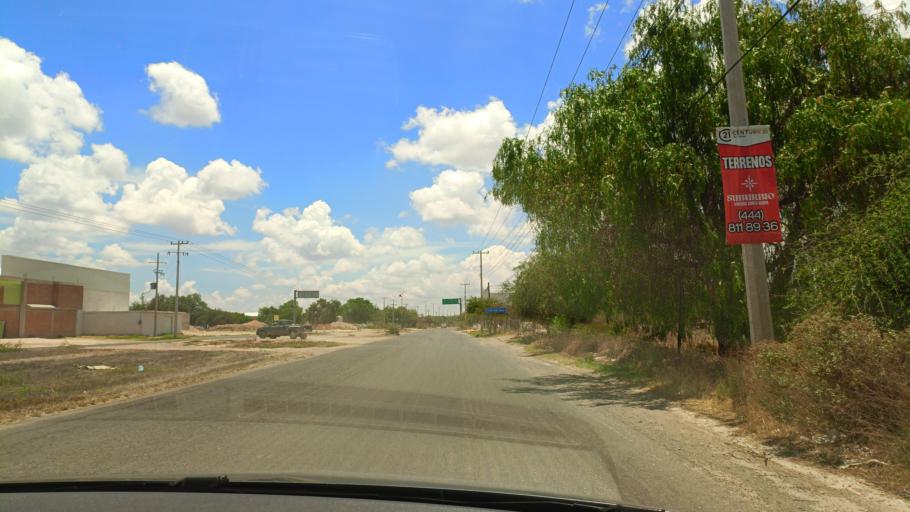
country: MX
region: Guanajuato
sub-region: San Luis de la Paz
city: San Ignacio
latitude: 21.2873
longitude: -100.5533
